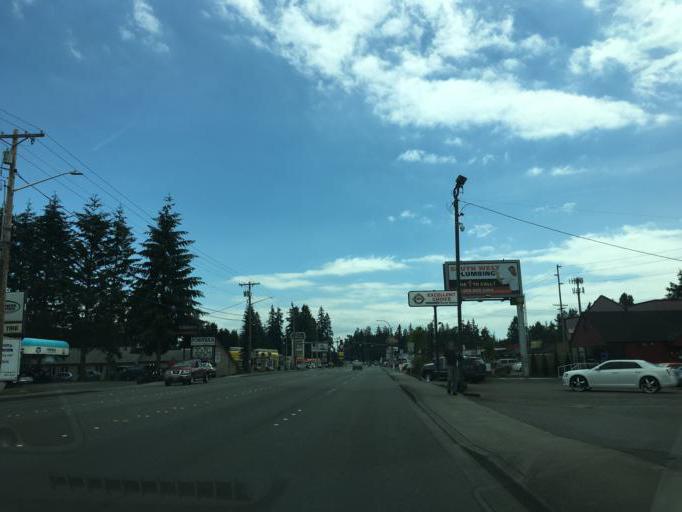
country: US
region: Washington
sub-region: Snohomish County
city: Marysville
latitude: 48.0805
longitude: -122.1746
